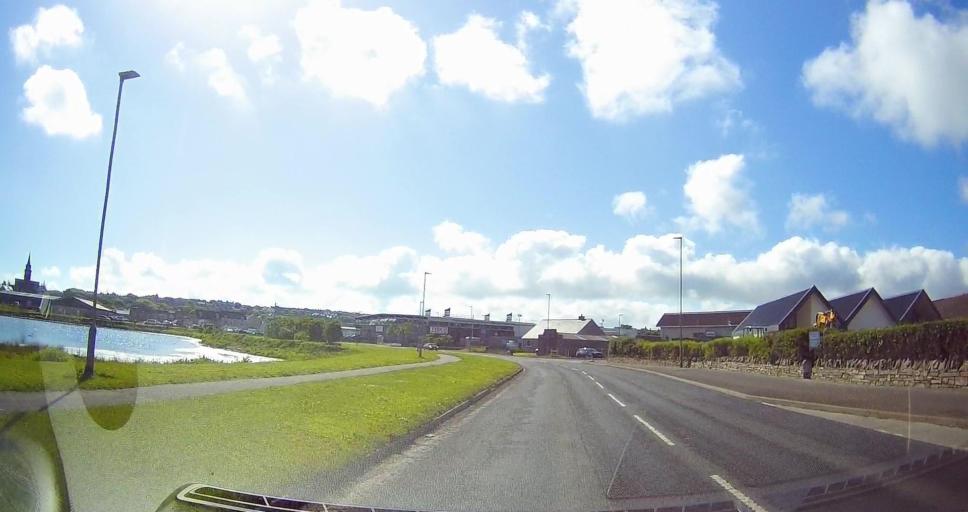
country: GB
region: Scotland
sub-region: Orkney Islands
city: Orkney
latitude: 58.9822
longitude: -2.9698
